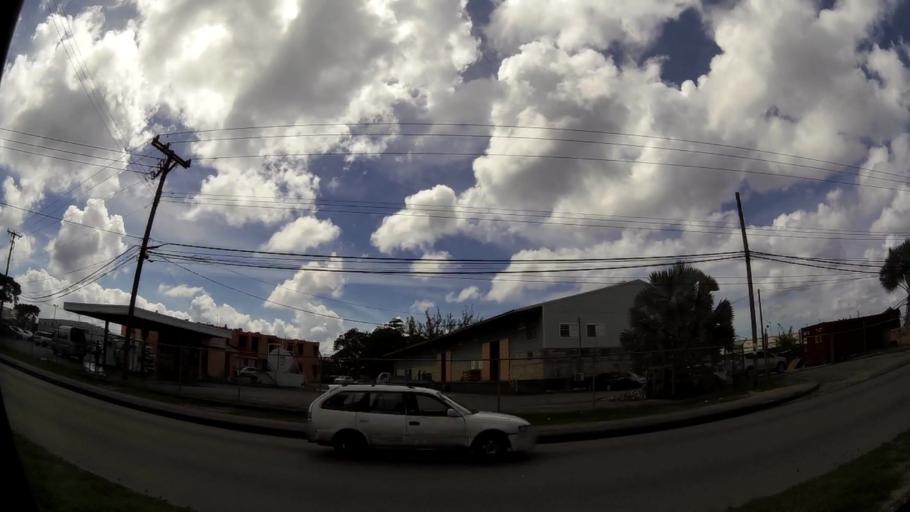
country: BB
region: Saint Michael
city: Bridgetown
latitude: 13.1068
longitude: -59.6243
